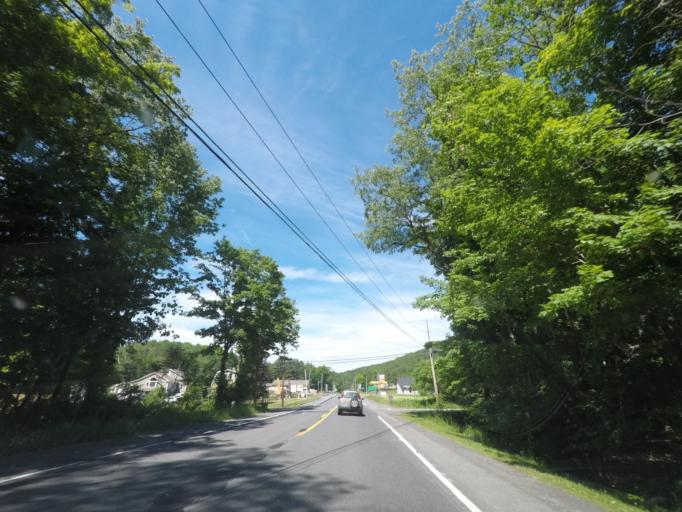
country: US
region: Massachusetts
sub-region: Berkshire County
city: Richmond
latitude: 42.3924
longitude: -73.4136
